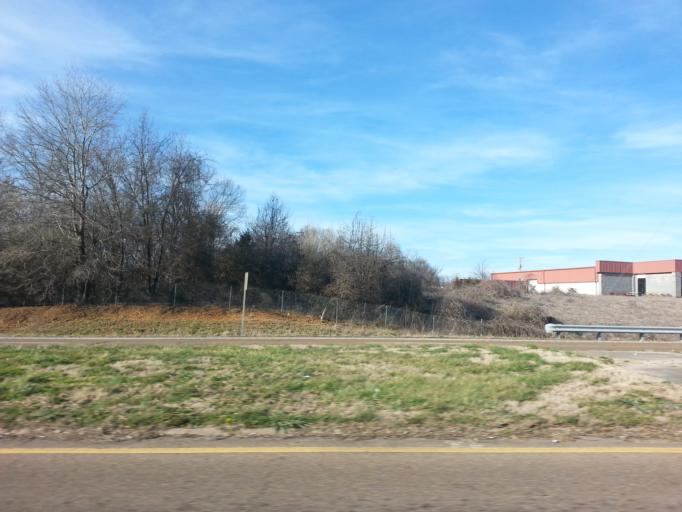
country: US
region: Tennessee
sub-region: Warren County
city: McMinnville
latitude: 35.6965
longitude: -85.7479
